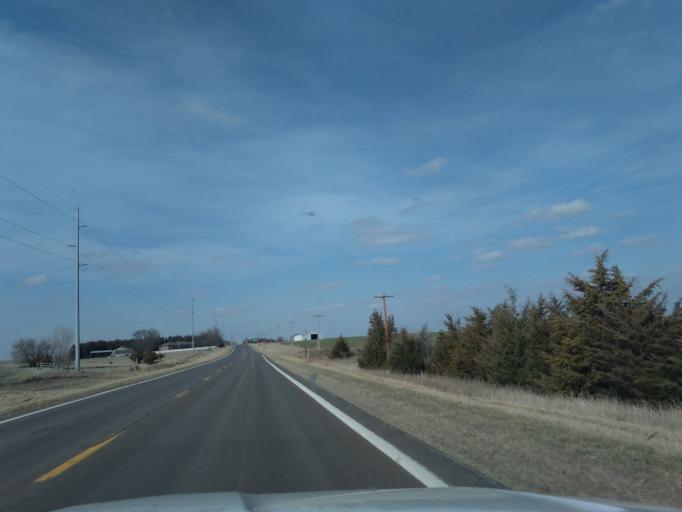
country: US
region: Nebraska
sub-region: Gage County
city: Beatrice
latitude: 40.2033
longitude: -96.9353
